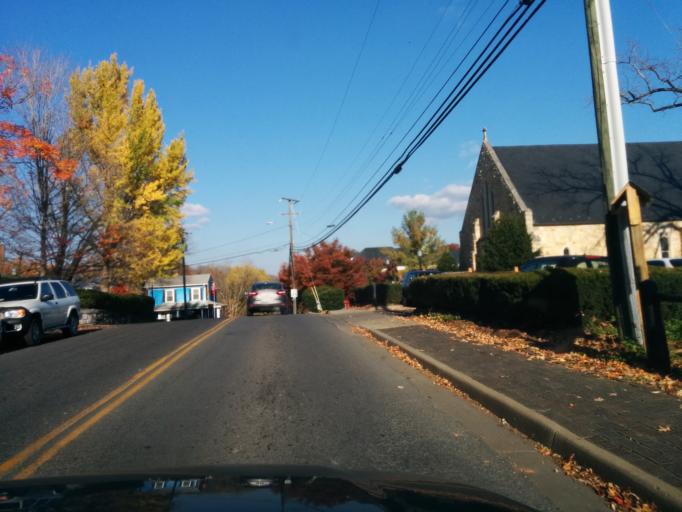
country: US
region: Virginia
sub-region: City of Lexington
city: Lexington
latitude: 37.7856
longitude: -79.4450
